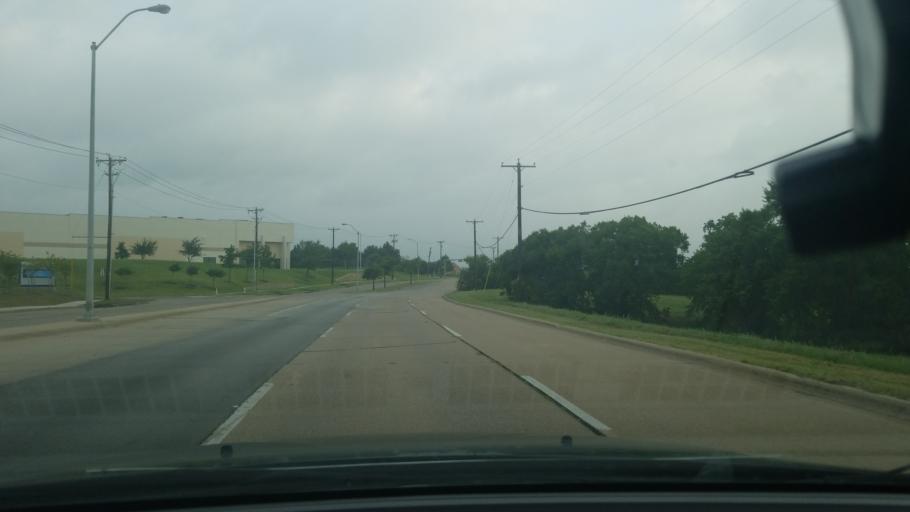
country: US
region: Texas
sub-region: Dallas County
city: Mesquite
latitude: 32.7767
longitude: -96.6289
